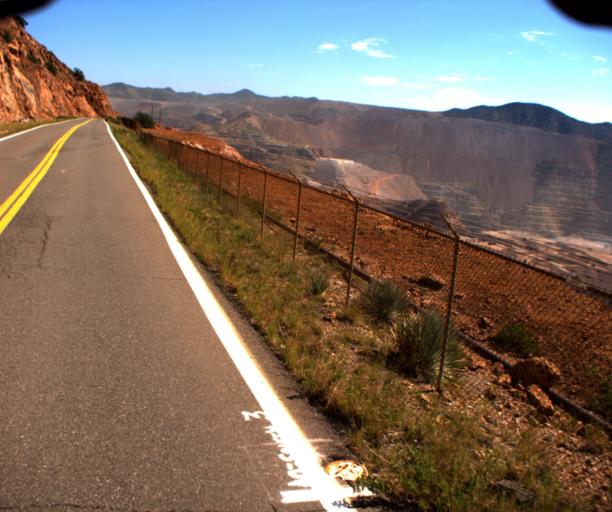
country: US
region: Arizona
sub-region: Greenlee County
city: Morenci
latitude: 33.0917
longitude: -109.3806
